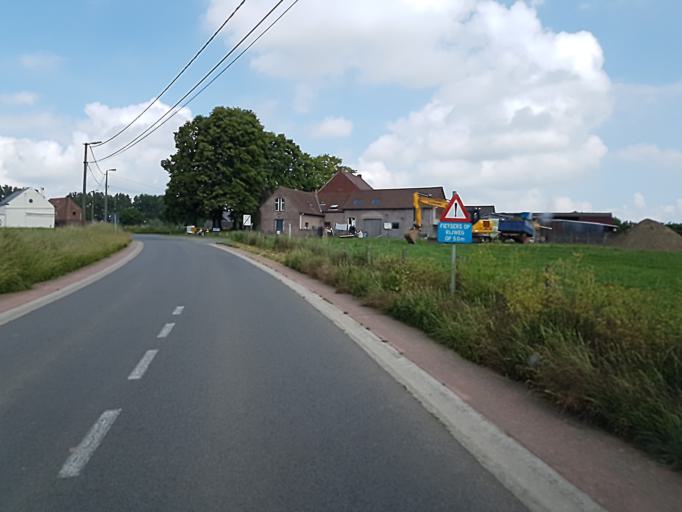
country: BE
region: Flanders
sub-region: Provincie Vlaams-Brabant
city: Herne
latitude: 50.7285
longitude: 4.0977
